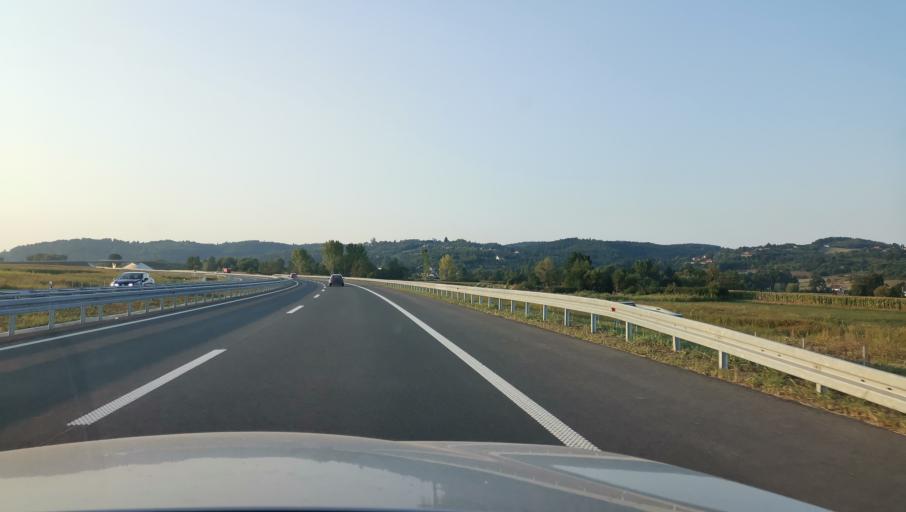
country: RS
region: Central Serbia
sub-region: Kolubarski Okrug
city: Lajkovac
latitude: 44.3257
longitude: 20.2128
